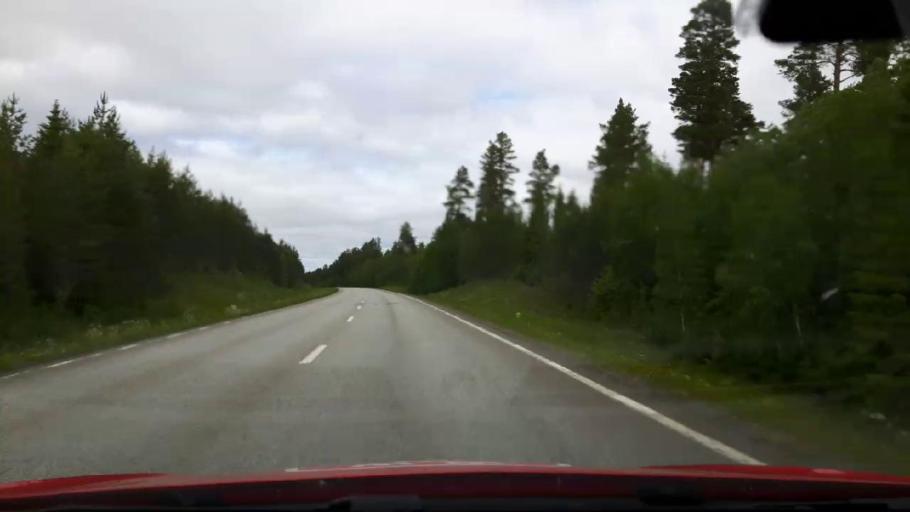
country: SE
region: Jaemtland
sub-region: Krokoms Kommun
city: Krokom
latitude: 63.4347
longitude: 14.4988
